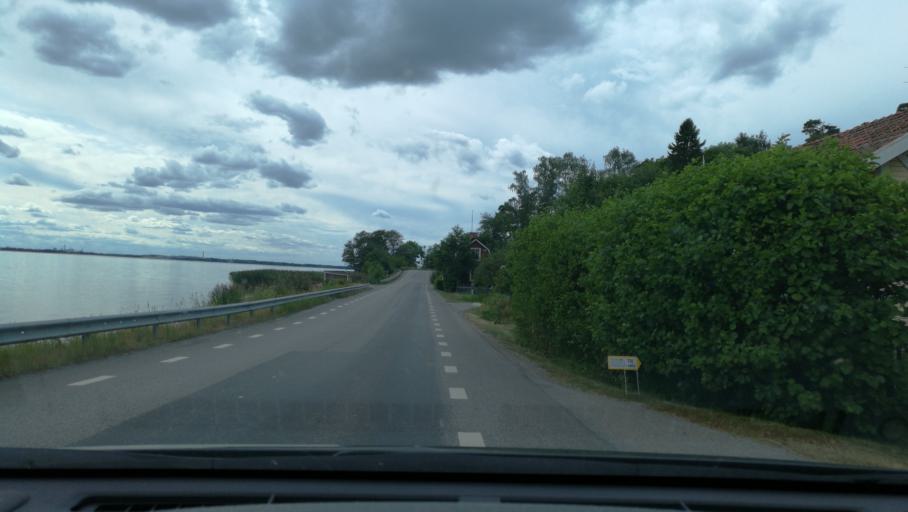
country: SE
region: OEstergoetland
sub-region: Norrkopings Kommun
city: Krokek
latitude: 58.6666
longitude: 16.3510
